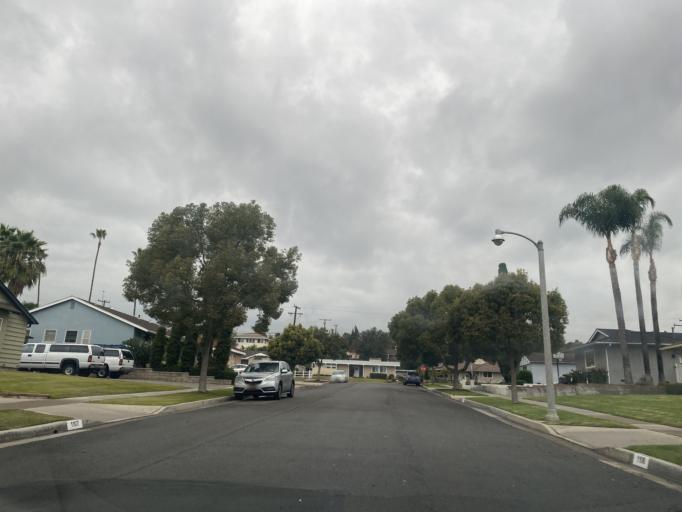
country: US
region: California
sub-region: Orange County
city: Fullerton
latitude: 33.8805
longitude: -117.9091
